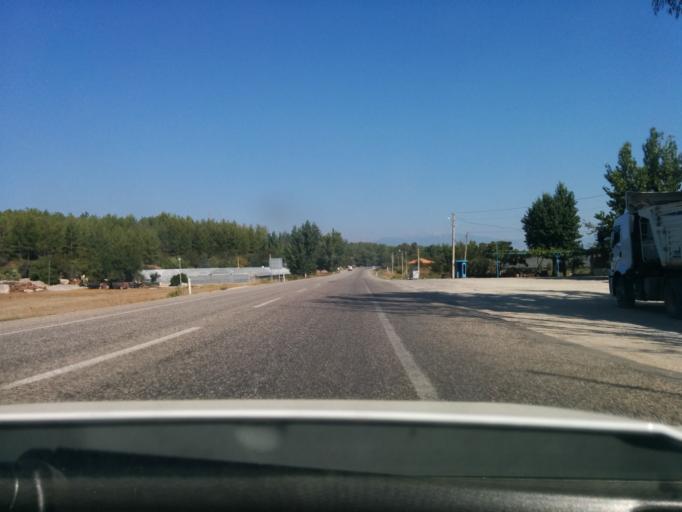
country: TR
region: Mugla
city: Kemer
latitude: 36.5452
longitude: 29.3446
